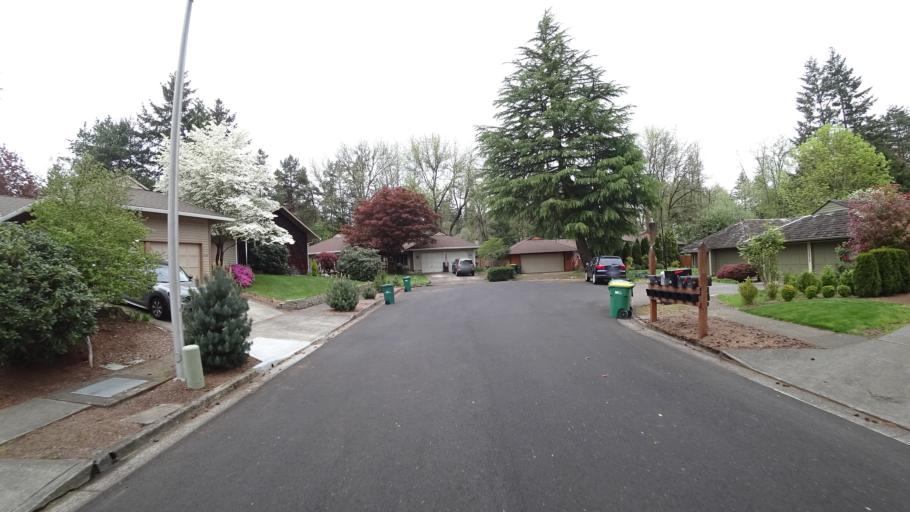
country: US
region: Oregon
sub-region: Washington County
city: Beaverton
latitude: 45.4563
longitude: -122.8197
